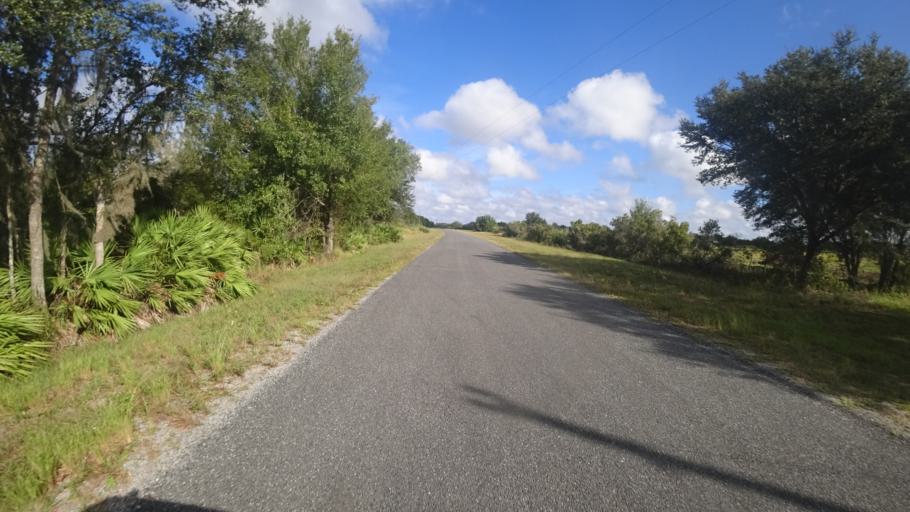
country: US
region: Florida
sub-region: Hillsborough County
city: Wimauma
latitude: 27.4859
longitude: -82.1538
